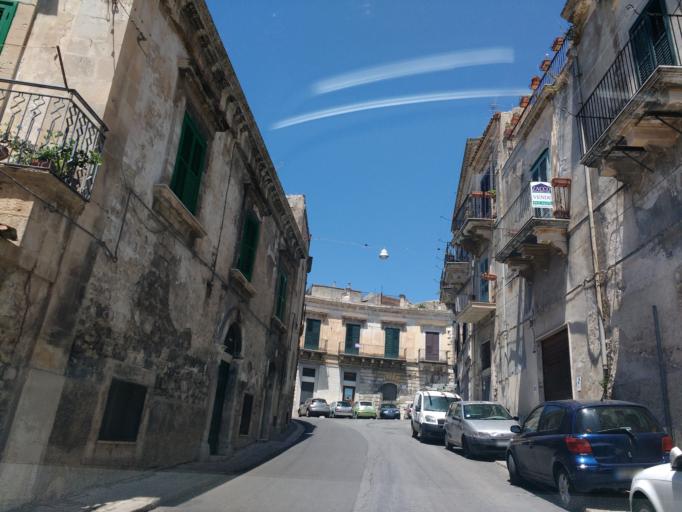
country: IT
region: Sicily
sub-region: Ragusa
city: Modica
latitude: 36.8641
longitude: 14.7622
